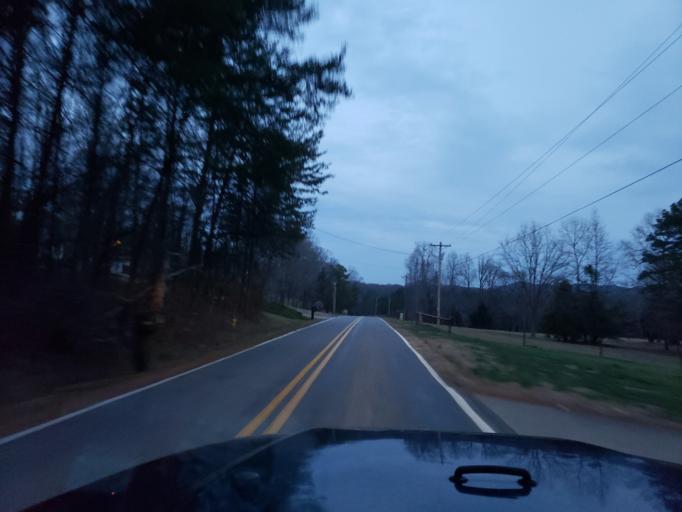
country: US
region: North Carolina
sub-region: Cleveland County
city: White Plains
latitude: 35.1682
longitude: -81.4050
